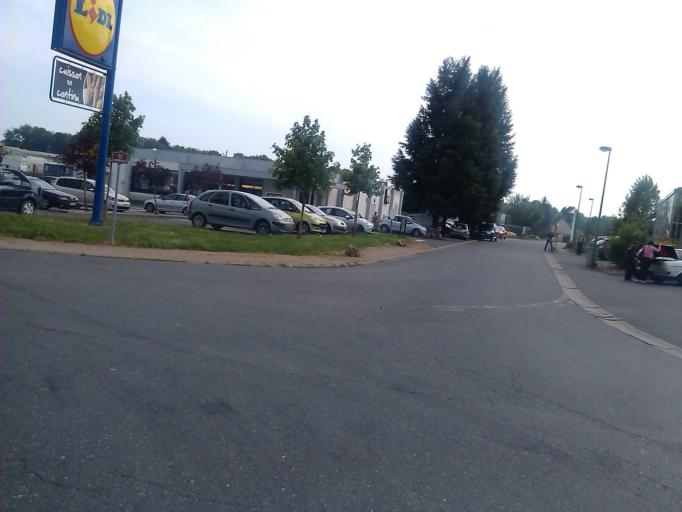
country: FR
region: Centre
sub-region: Departement de l'Indre
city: La Chatre
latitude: 46.5823
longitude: 2.0005
